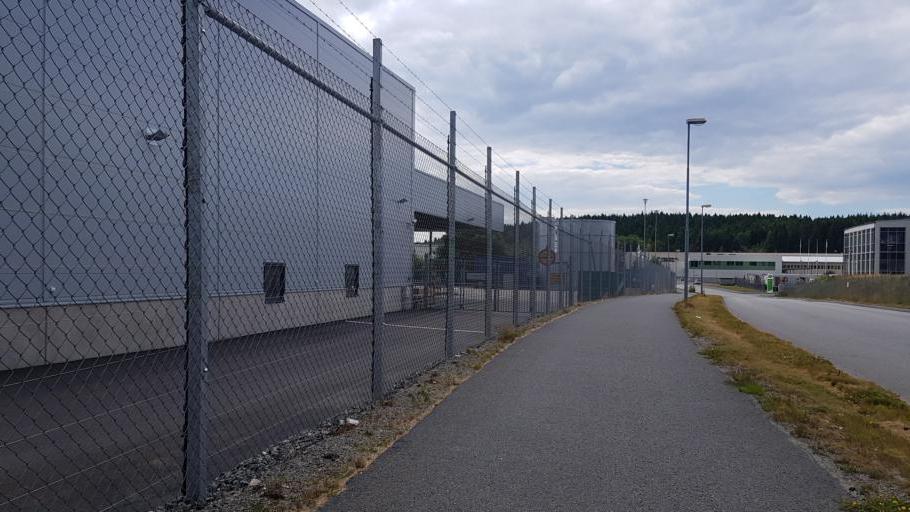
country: SE
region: Vaestra Goetaland
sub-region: Harryda Kommun
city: Molnlycke
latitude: 57.6755
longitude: 12.0921
